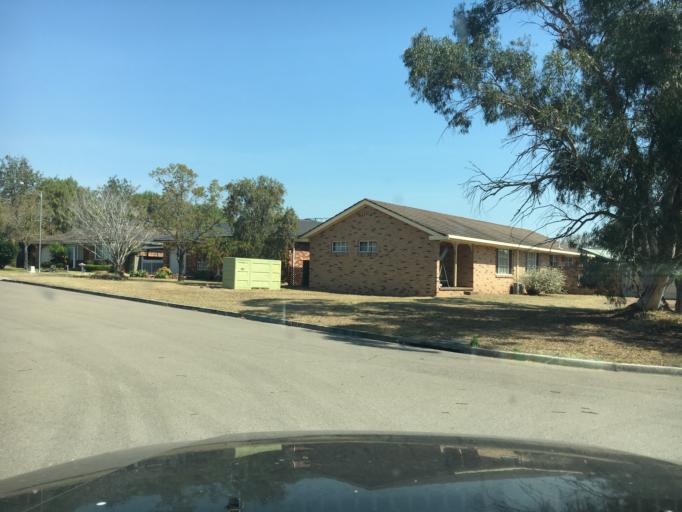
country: AU
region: New South Wales
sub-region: Singleton
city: Singleton
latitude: -32.5684
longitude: 151.1896
